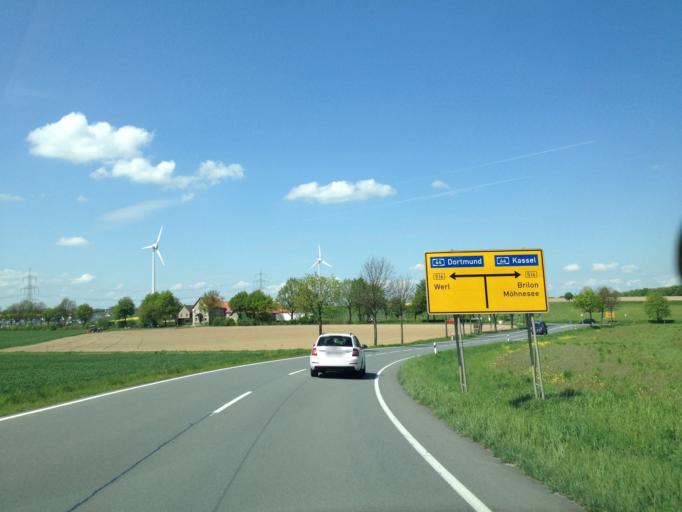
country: DE
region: North Rhine-Westphalia
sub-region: Regierungsbezirk Arnsberg
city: Werl
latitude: 51.5017
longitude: 7.9815
